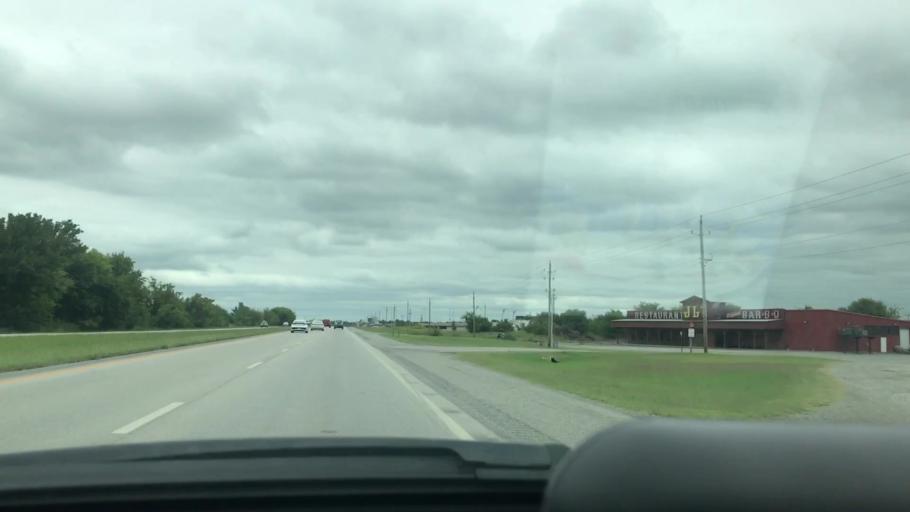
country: US
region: Oklahoma
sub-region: Mayes County
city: Pryor
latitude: 36.2546
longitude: -95.3348
